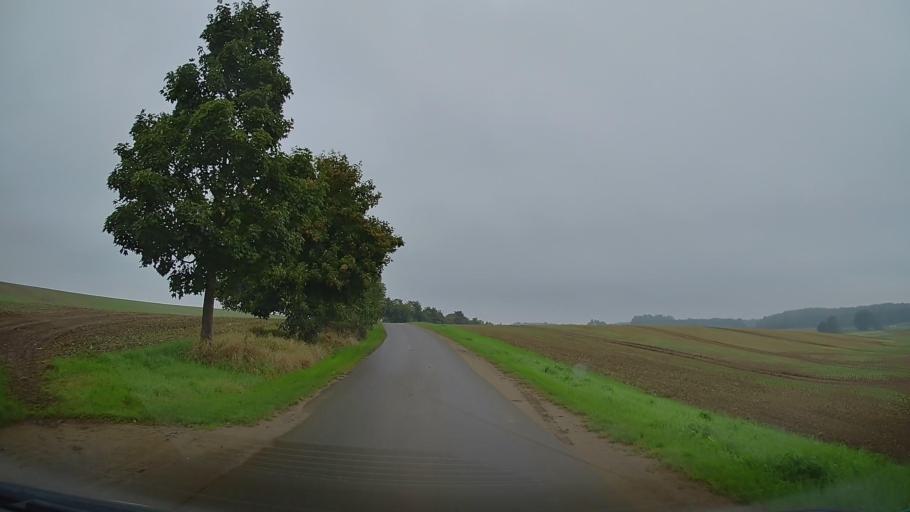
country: DE
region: Mecklenburg-Vorpommern
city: Gramkow
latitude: 53.9203
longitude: 11.3498
